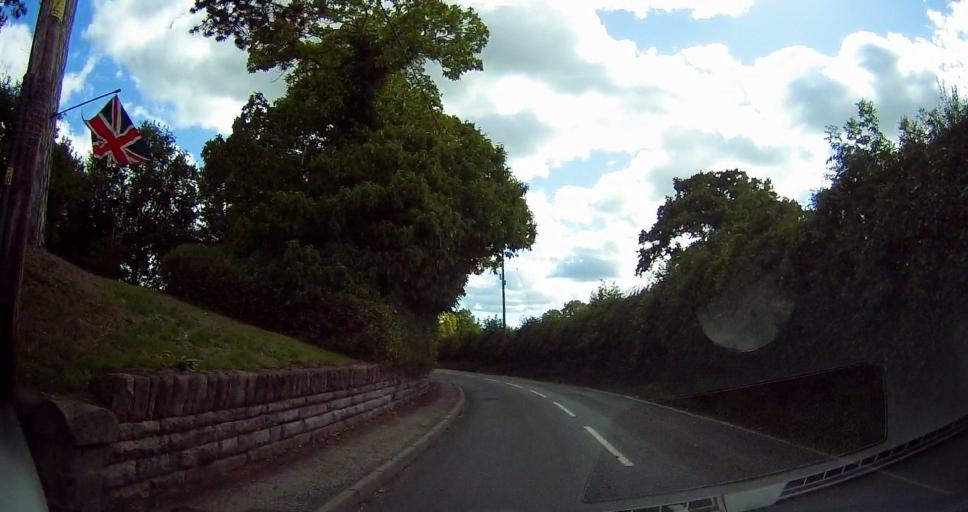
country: GB
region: England
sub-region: Cheshire East
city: Willaston
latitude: 52.9873
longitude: -2.4981
